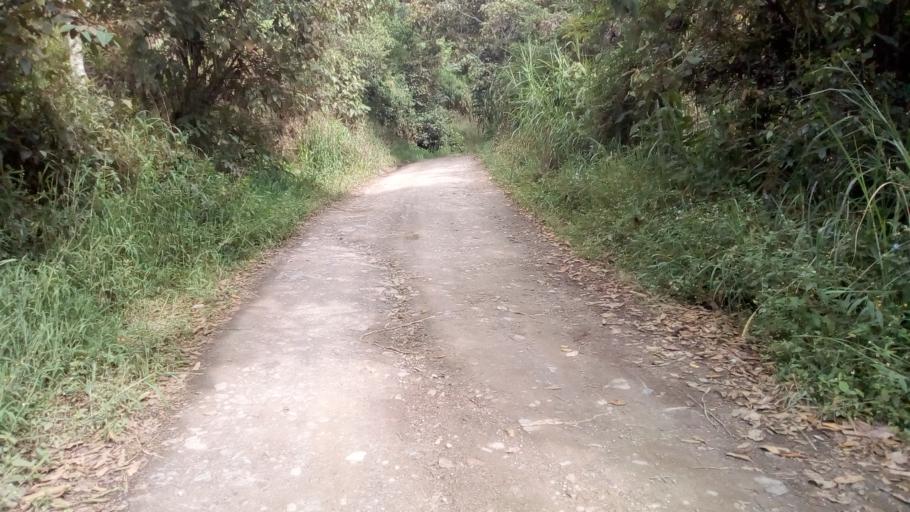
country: CO
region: Cundinamarca
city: Tenza
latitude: 5.0972
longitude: -73.4178
